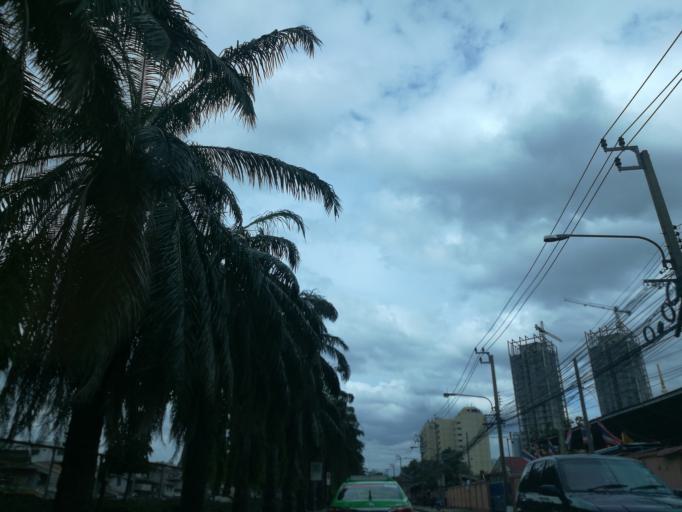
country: TH
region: Bangkok
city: Bang Sue
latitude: 13.7993
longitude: 100.5334
